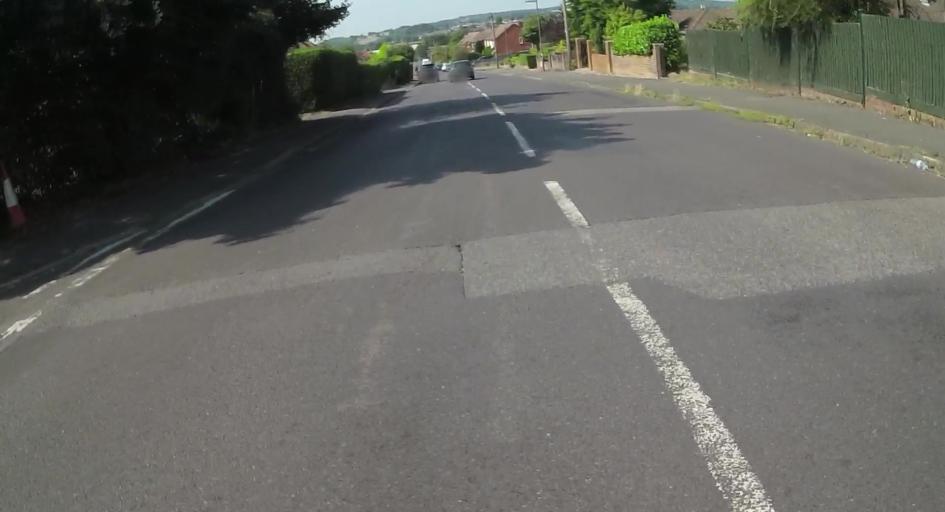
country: GB
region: England
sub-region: Surrey
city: Farnham
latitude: 51.2015
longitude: -0.8075
